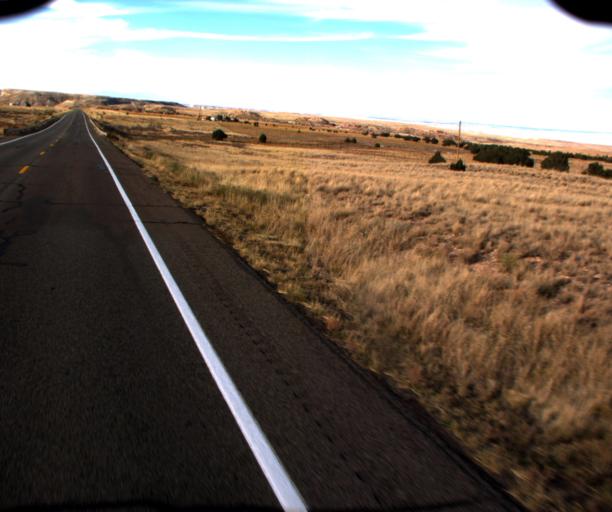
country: US
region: New Mexico
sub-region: San Juan County
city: Shiprock
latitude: 36.9034
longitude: -109.0686
